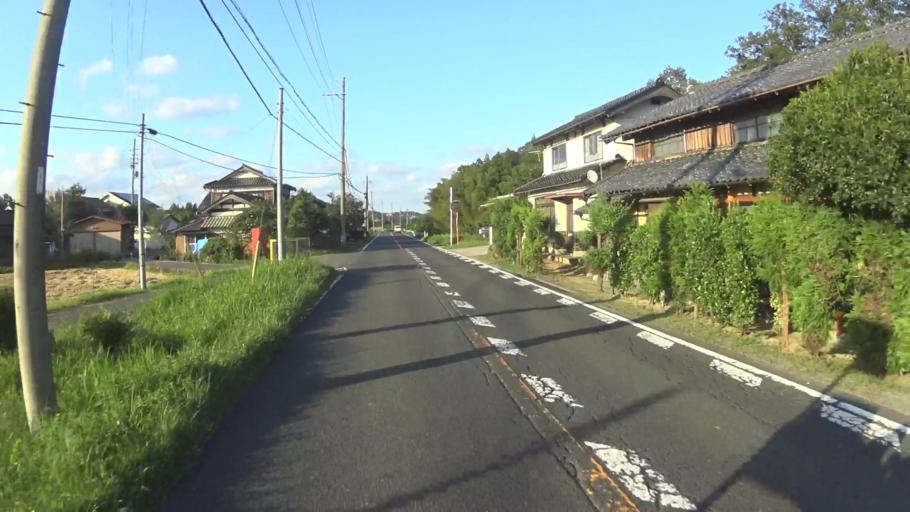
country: JP
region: Kyoto
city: Miyazu
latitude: 35.5947
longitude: 135.0434
